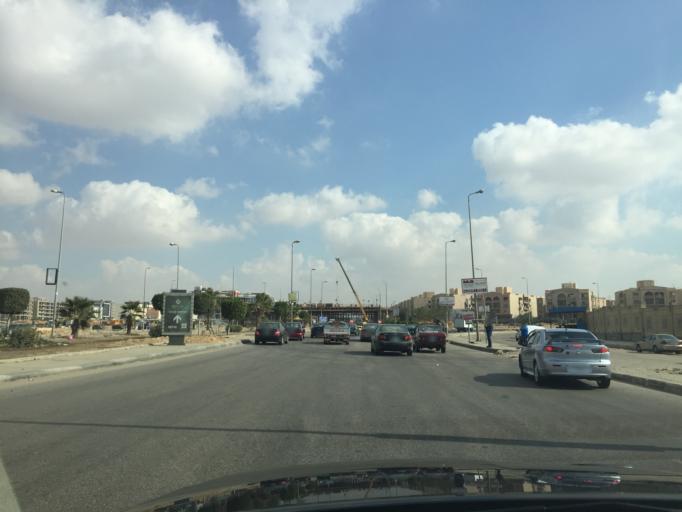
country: EG
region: Muhafazat al Qalyubiyah
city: Al Khankah
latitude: 30.0253
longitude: 31.4727
